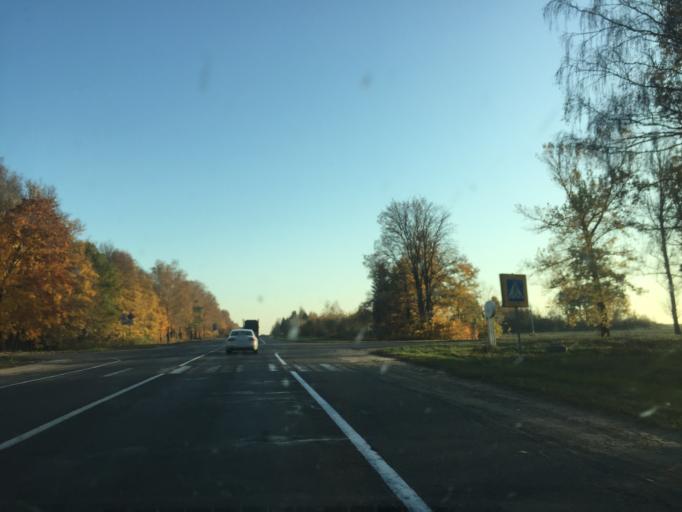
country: BY
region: Mogilev
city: Poselok Voskhod
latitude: 53.7537
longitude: 30.3653
